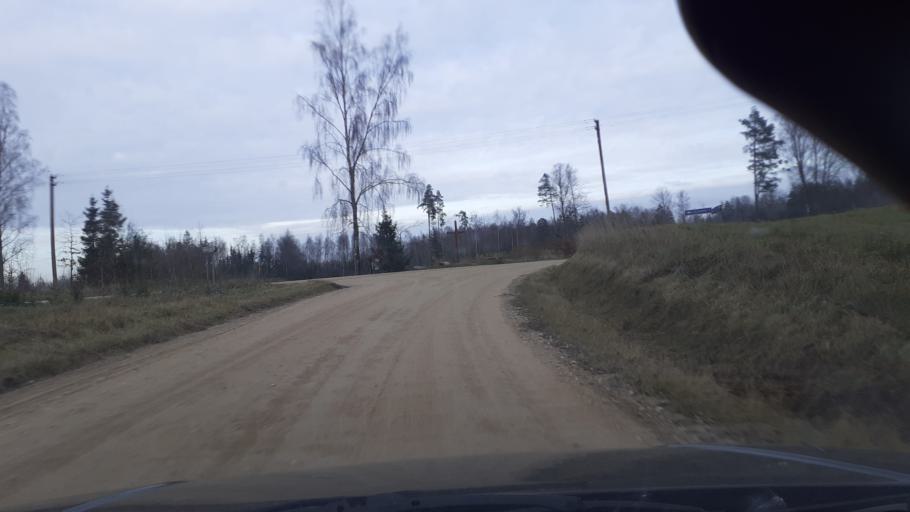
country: LV
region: Alsunga
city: Alsunga
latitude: 56.9683
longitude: 21.6577
